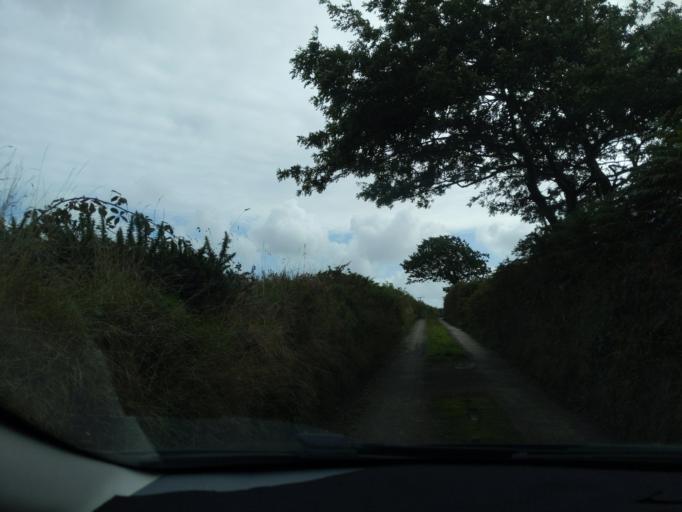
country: GB
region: England
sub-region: Cornwall
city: Par
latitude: 50.3895
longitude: -4.7031
